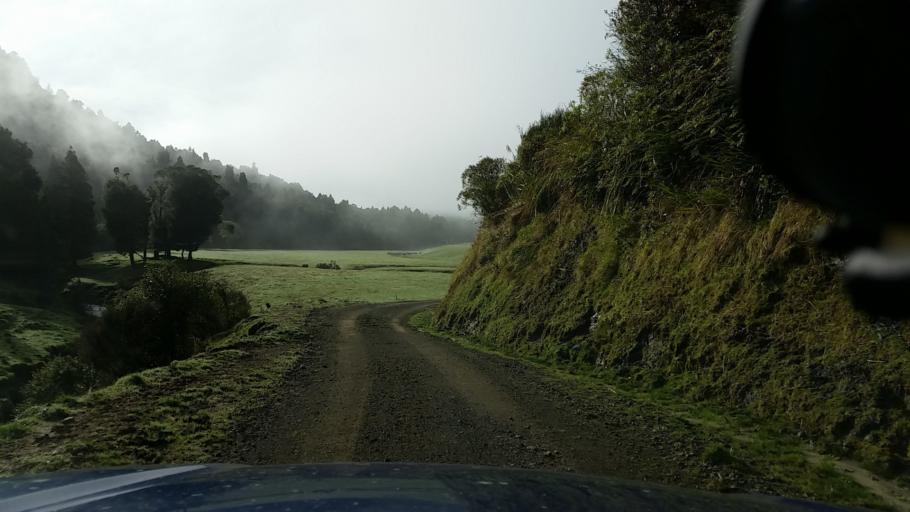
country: NZ
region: Taranaki
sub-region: New Plymouth District
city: Waitara
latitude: -38.9782
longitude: 174.7493
